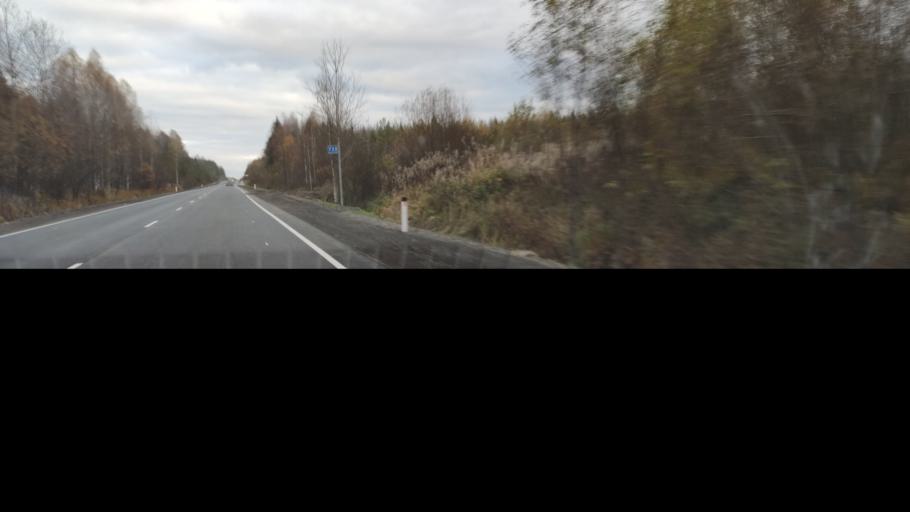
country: RU
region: Kirov
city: Chernaya Kholunitsa
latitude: 58.8710
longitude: 51.5349
